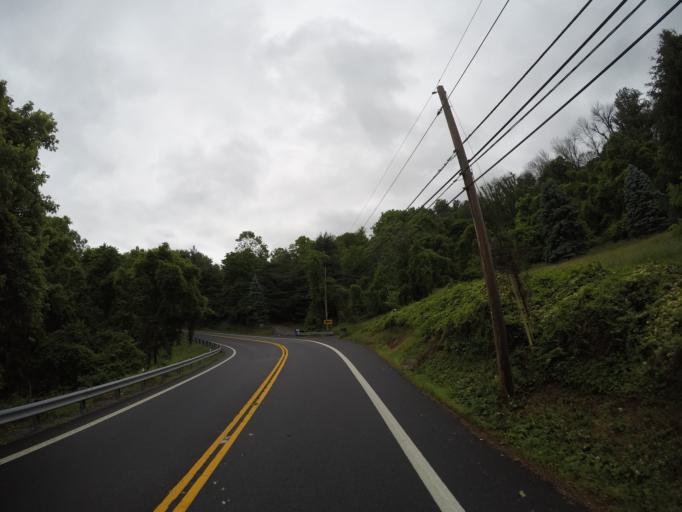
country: US
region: Maryland
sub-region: Washington County
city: Boonsboro
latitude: 39.4788
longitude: -77.6118
